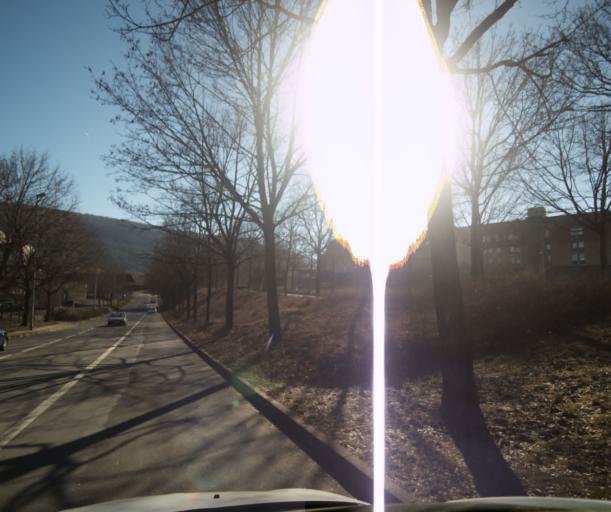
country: FR
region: Franche-Comte
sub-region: Departement du Doubs
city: Avanne-Aveney
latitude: 47.2188
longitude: 5.9759
